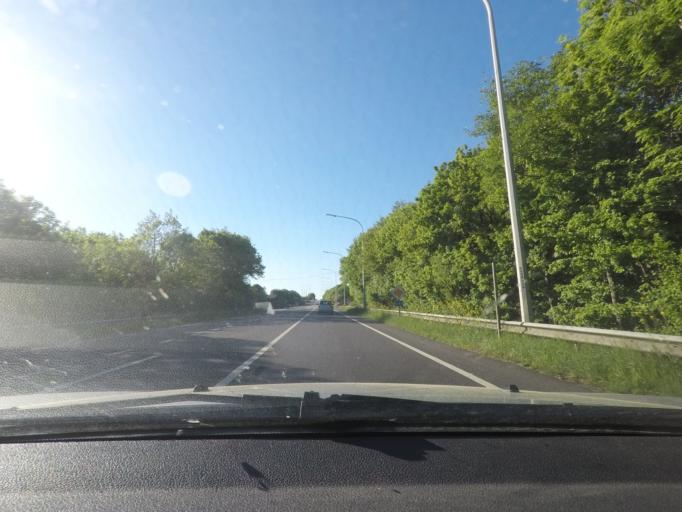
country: BE
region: Wallonia
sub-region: Province de Namur
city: Houyet
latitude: 50.1659
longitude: 5.0750
